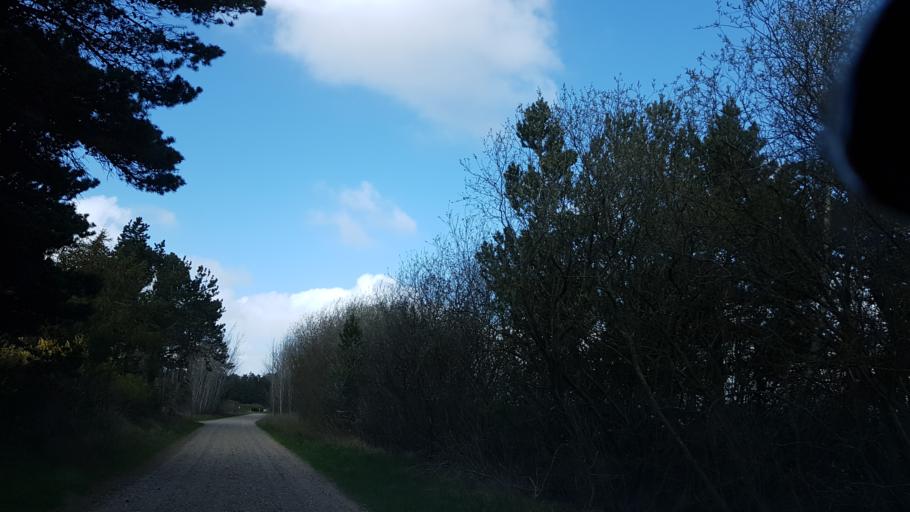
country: DE
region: Schleswig-Holstein
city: List
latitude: 55.0837
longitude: 8.5389
